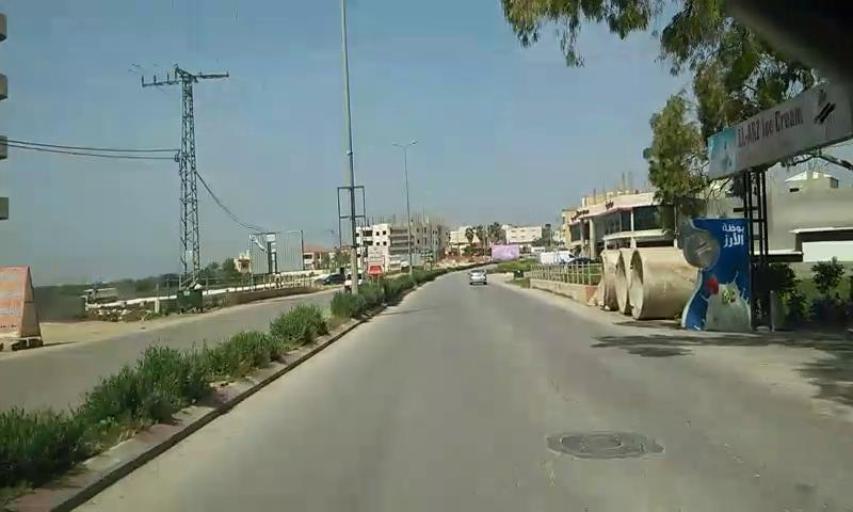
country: PS
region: West Bank
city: Janin
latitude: 32.4802
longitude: 35.2996
